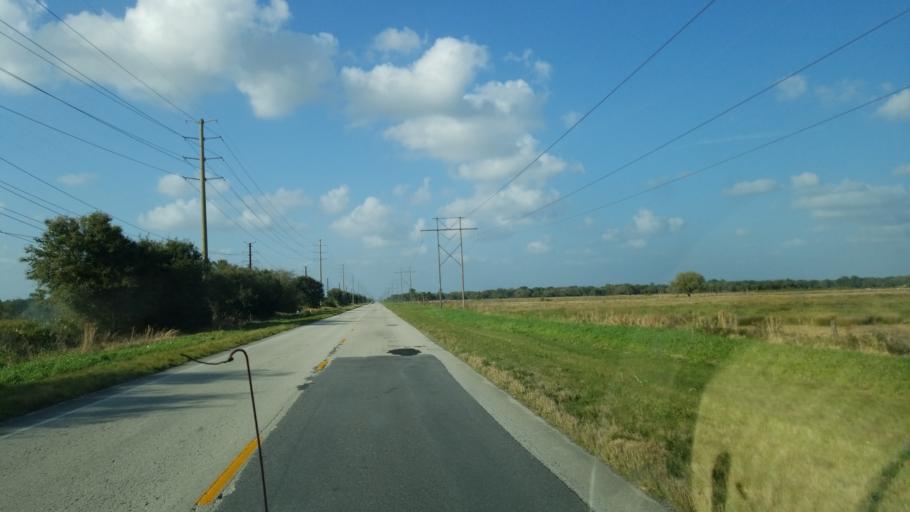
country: US
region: Florida
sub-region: Hardee County
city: Wauchula
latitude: 27.5286
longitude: -81.9277
